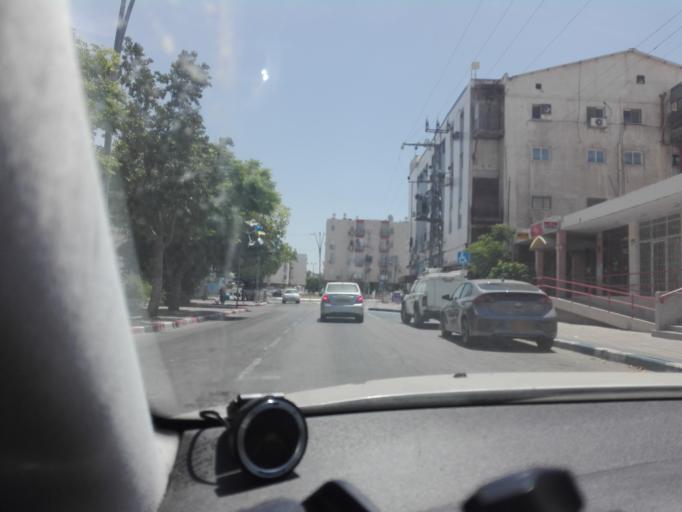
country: IL
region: Central District
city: Bene 'Ayish
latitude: 31.7288
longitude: 34.7486
